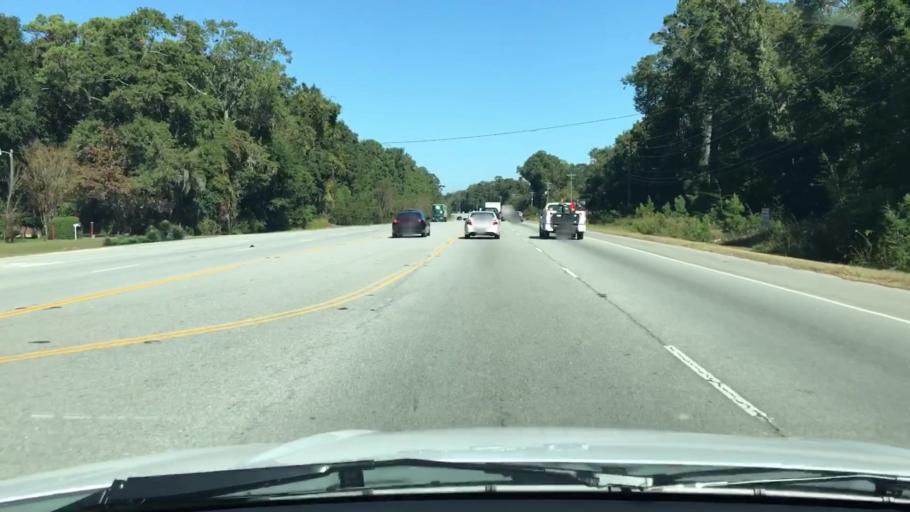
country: US
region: South Carolina
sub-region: Beaufort County
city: Shell Point
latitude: 32.3974
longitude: -80.7651
